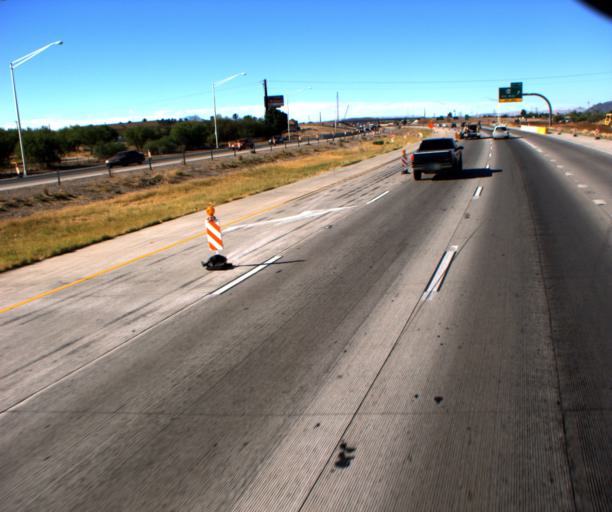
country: US
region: Arizona
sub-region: Pima County
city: South Tucson
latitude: 32.1834
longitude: -110.9852
